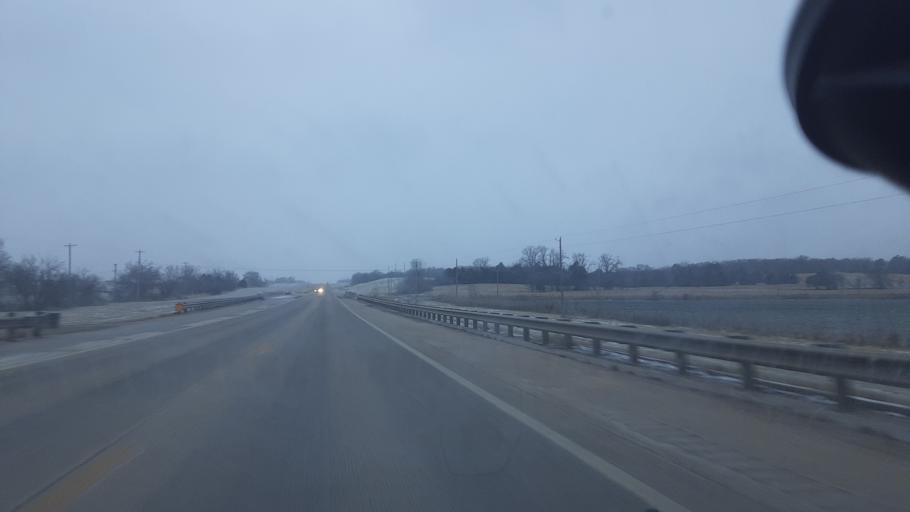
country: US
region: Oklahoma
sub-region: Payne County
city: Perkins
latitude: 35.9859
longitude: -97.1203
